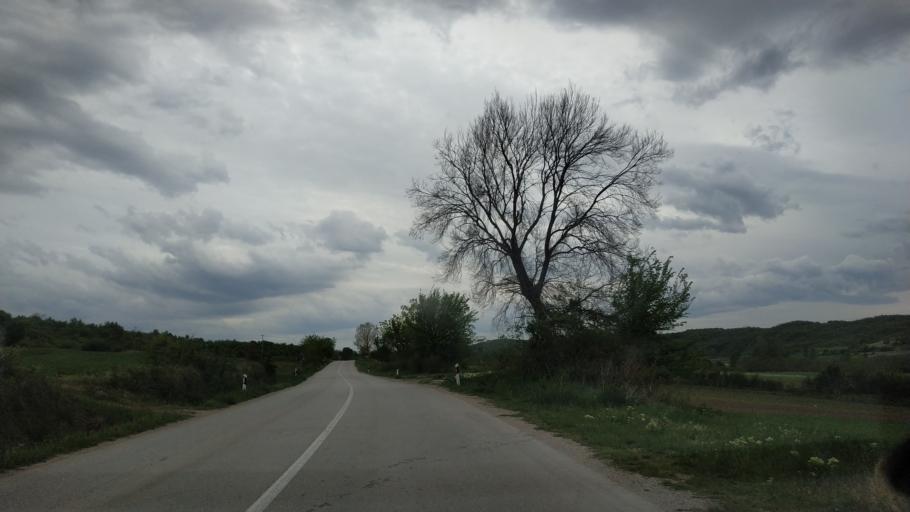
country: RS
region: Central Serbia
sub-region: Nisavski Okrug
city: Aleksinac
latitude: 43.6180
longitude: 21.6914
